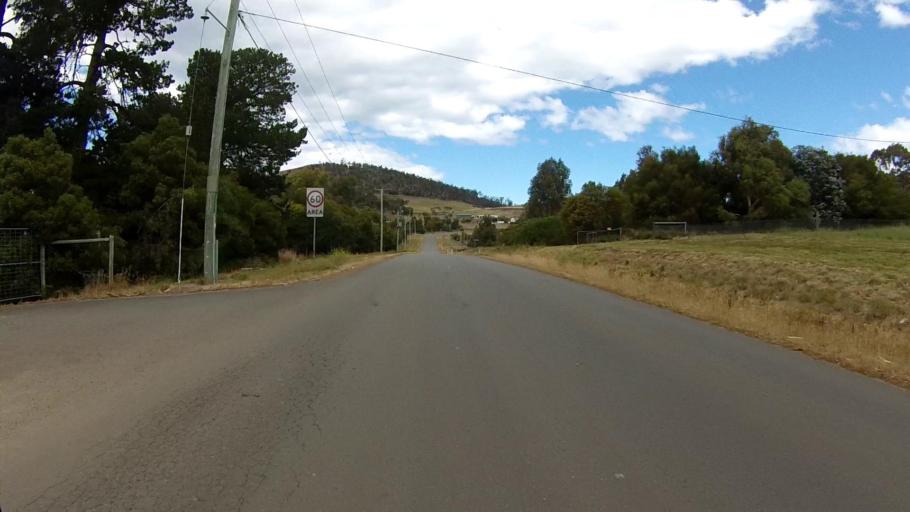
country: AU
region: Tasmania
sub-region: Clarence
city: Acton Park
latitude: -42.8680
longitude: 147.4872
